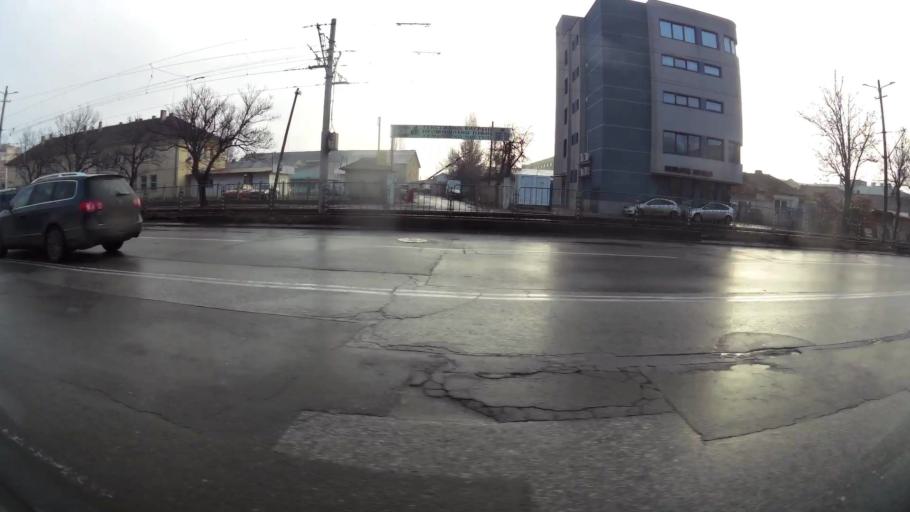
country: BG
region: Sofia-Capital
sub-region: Stolichna Obshtina
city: Sofia
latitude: 42.7303
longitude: 23.3130
